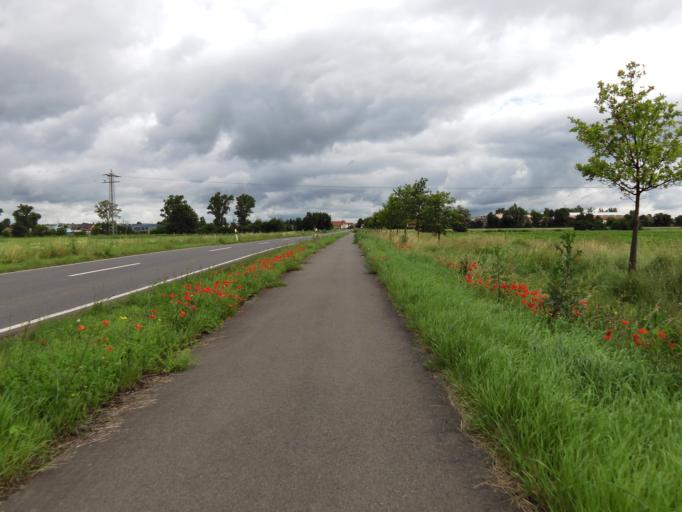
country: DE
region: Rheinland-Pfalz
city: Gerolsheim
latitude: 49.5559
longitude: 8.2604
